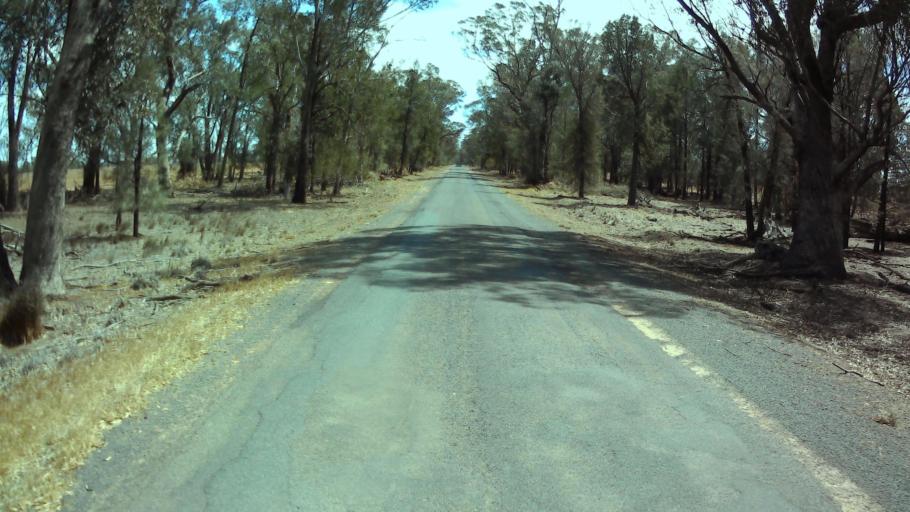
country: AU
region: New South Wales
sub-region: Weddin
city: Grenfell
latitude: -33.6519
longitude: 148.1953
